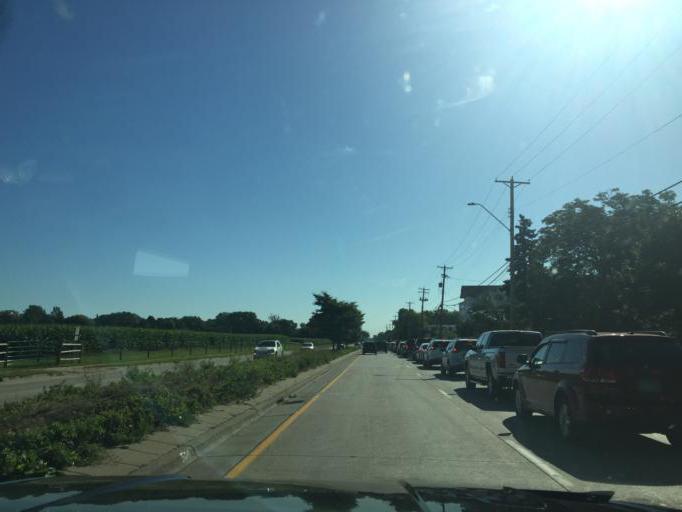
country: US
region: Minnesota
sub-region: Ramsey County
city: Falcon Heights
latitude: 44.9917
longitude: -93.1760
